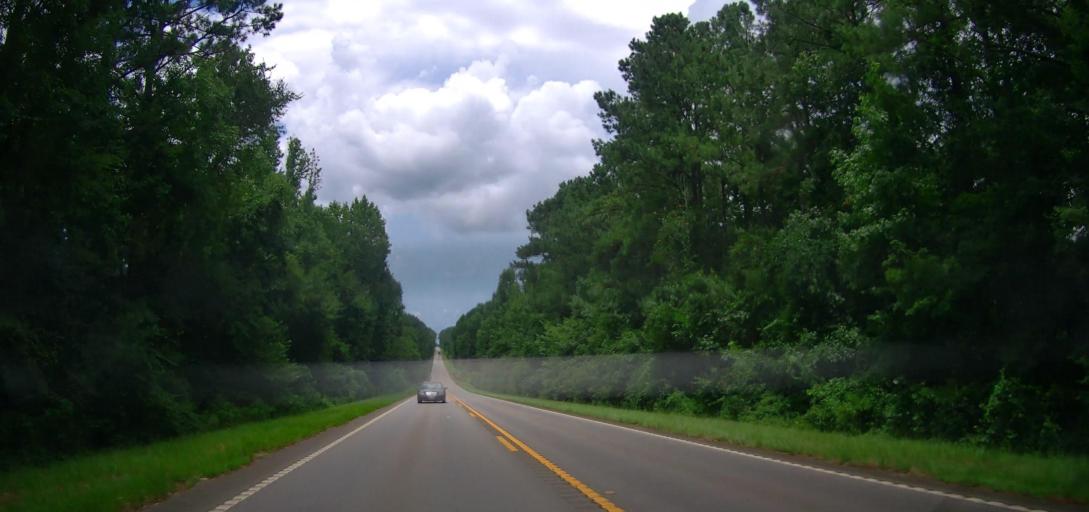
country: US
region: Georgia
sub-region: Pulaski County
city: Hawkinsville
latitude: 32.3789
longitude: -83.5490
